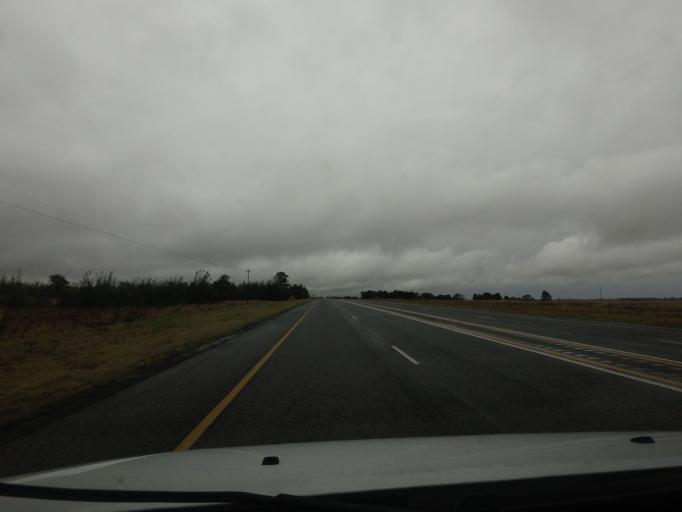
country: ZA
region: Mpumalanga
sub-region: Nkangala District Municipality
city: Belfast
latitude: -25.7936
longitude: 29.9167
